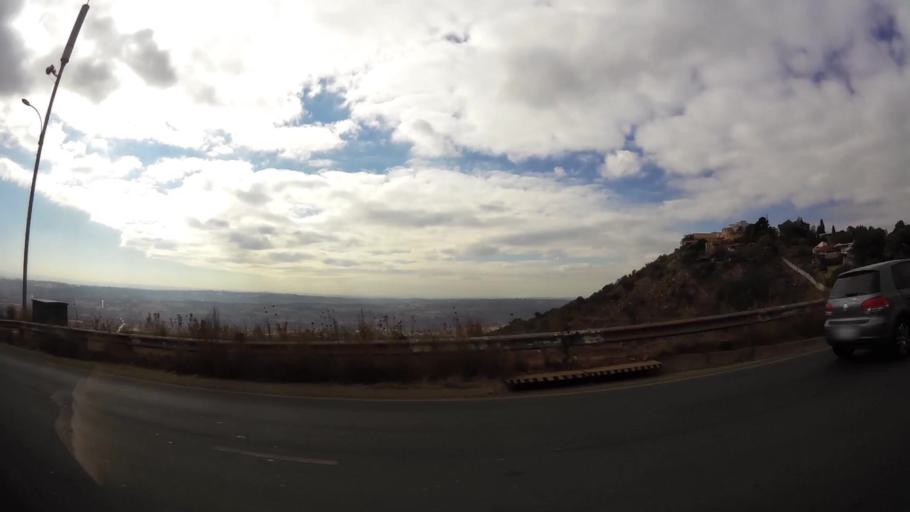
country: ZA
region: Gauteng
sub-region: City of Johannesburg Metropolitan Municipality
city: Roodepoort
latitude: -26.1063
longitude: 27.8669
